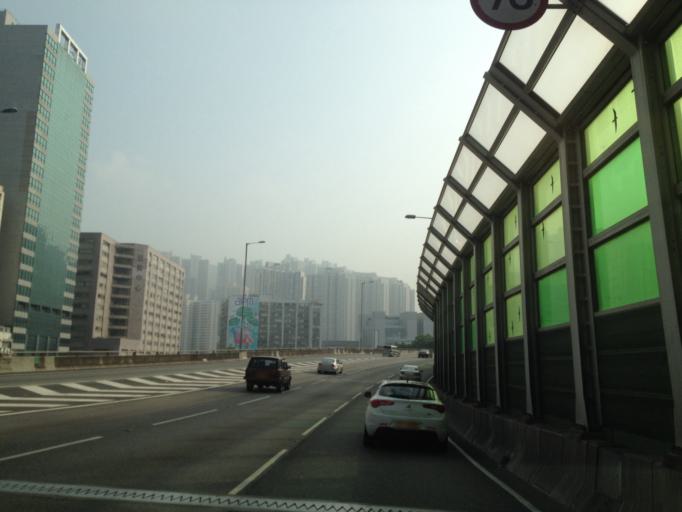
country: HK
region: Kowloon City
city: Kowloon
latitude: 22.3079
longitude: 114.2261
